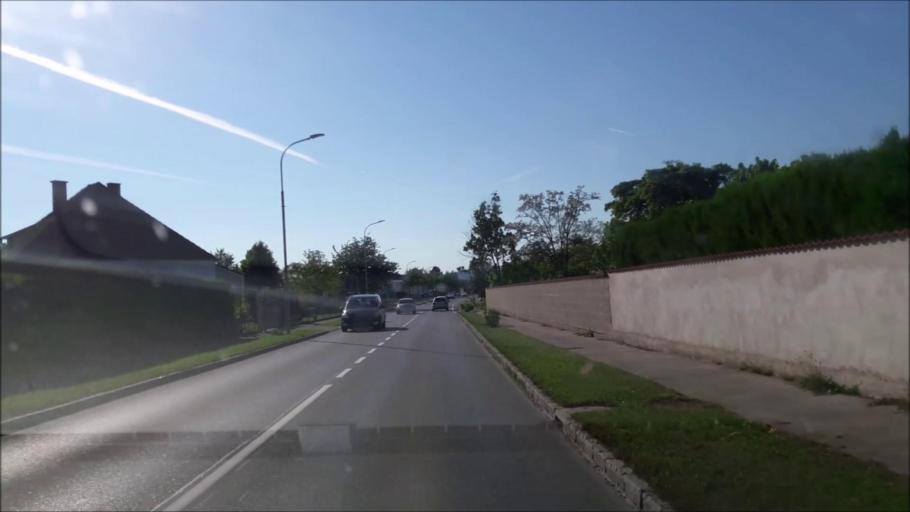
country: AT
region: Burgenland
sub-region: Eisenstadt-Umgebung
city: Trausdorf an der Wulka
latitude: 47.8135
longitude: 16.5520
